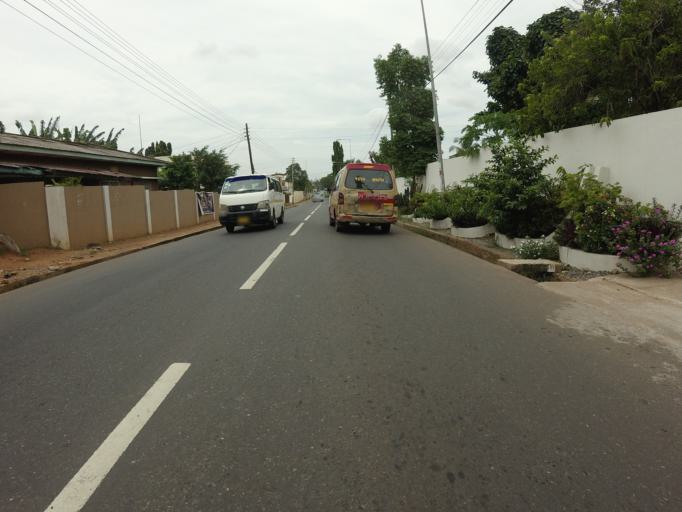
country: GH
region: Greater Accra
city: Dome
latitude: 5.5986
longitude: -0.2293
